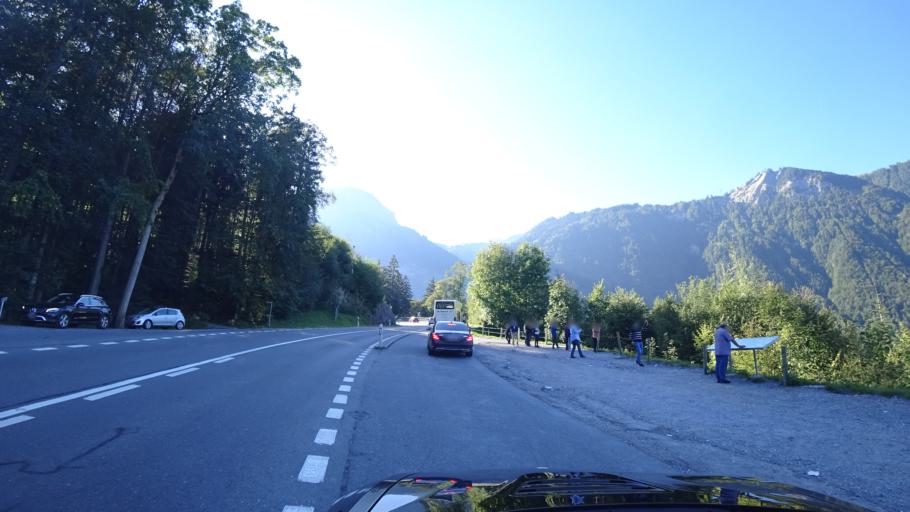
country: CH
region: Obwalden
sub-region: Obwalden
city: Lungern
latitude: 46.7757
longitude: 8.1434
